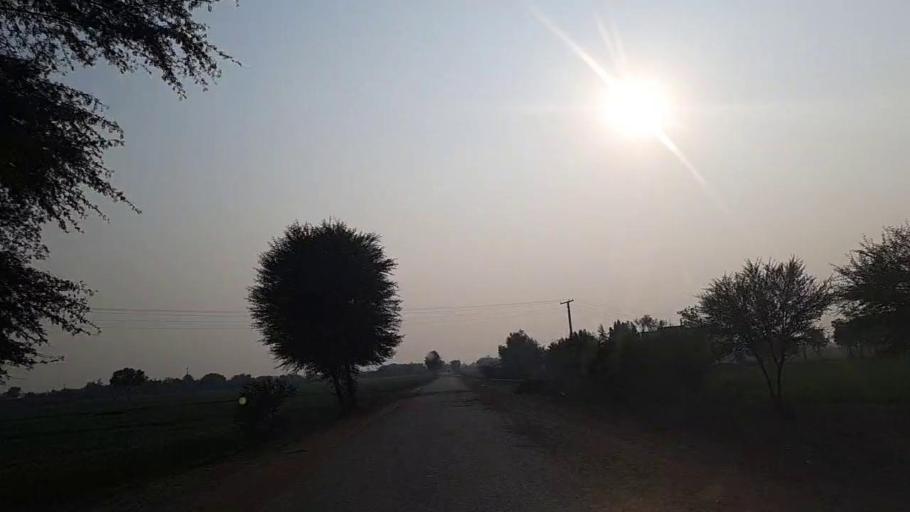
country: PK
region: Sindh
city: Nawabshah
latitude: 26.2214
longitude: 68.4764
